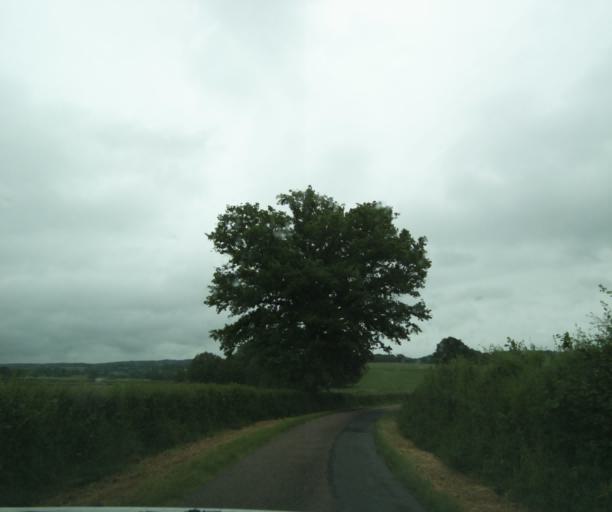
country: FR
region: Bourgogne
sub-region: Departement de Saone-et-Loire
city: Palinges
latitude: 46.4935
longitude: 4.2352
